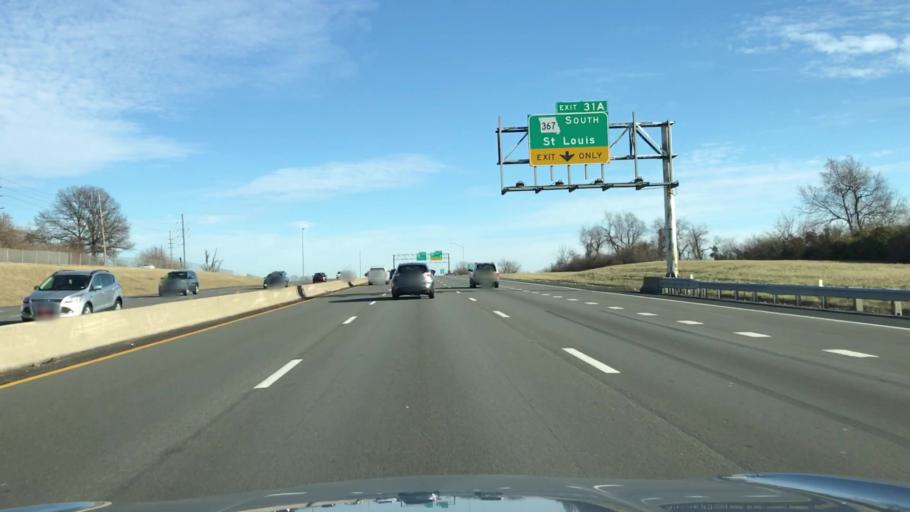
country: US
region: Missouri
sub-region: Saint Louis County
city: Castle Point
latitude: 38.7707
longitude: -90.2462
